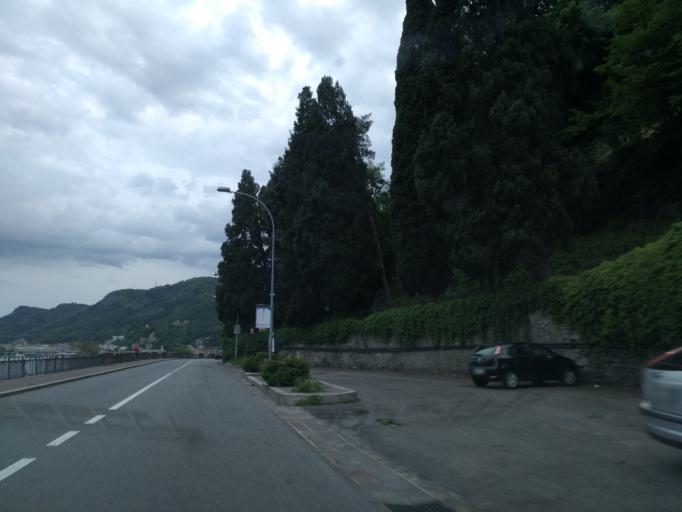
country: IT
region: Lombardy
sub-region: Provincia di Como
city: Cernobbio
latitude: 45.8254
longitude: 9.0685
